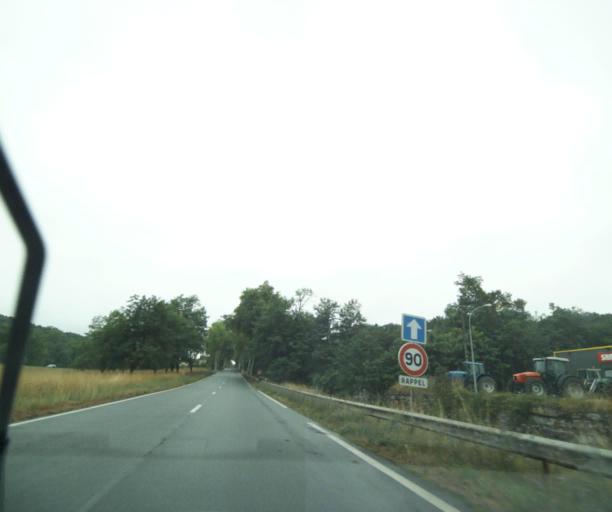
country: FR
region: Midi-Pyrenees
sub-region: Departement du Tarn
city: Arthes
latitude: 43.9721
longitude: 2.1825
